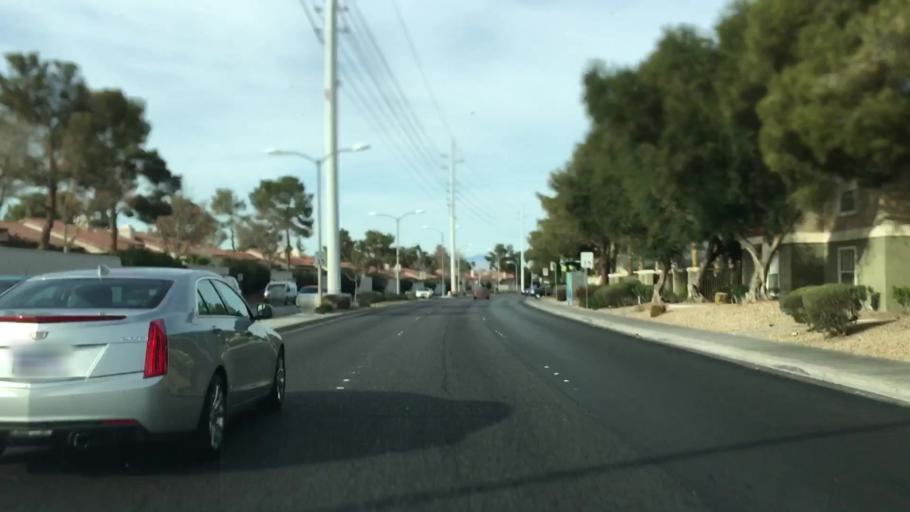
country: US
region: Nevada
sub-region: Clark County
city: Whitney
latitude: 36.0568
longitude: -115.0843
